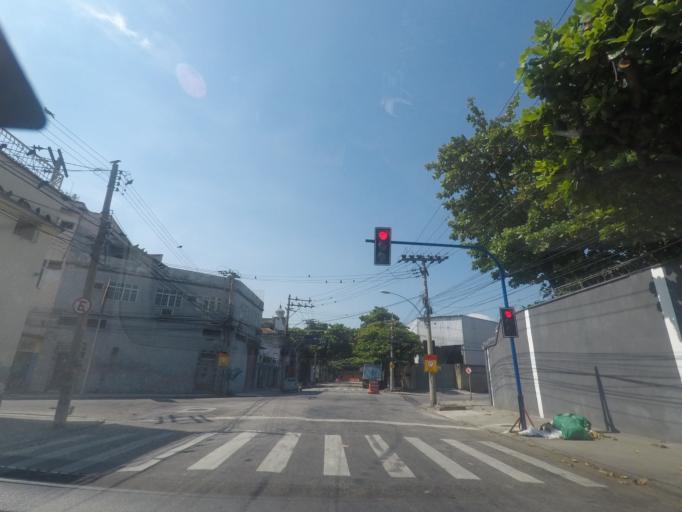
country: BR
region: Rio de Janeiro
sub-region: Rio De Janeiro
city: Rio de Janeiro
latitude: -22.8908
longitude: -43.2192
